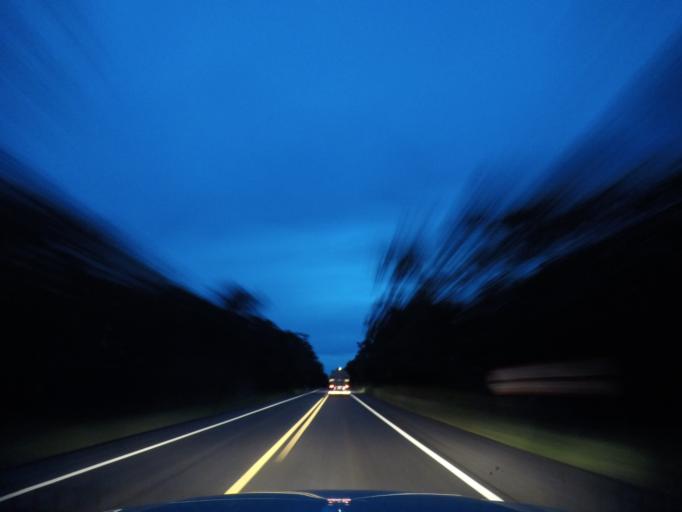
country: BR
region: Bahia
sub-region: Andarai
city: Vera Cruz
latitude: -12.4829
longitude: -41.3492
